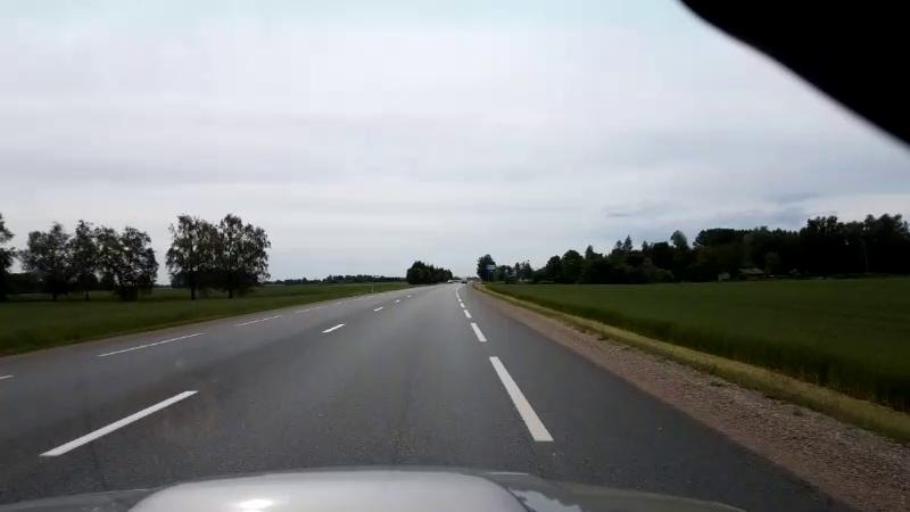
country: LV
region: Bauskas Rajons
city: Bauska
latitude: 56.4522
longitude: 24.1638
